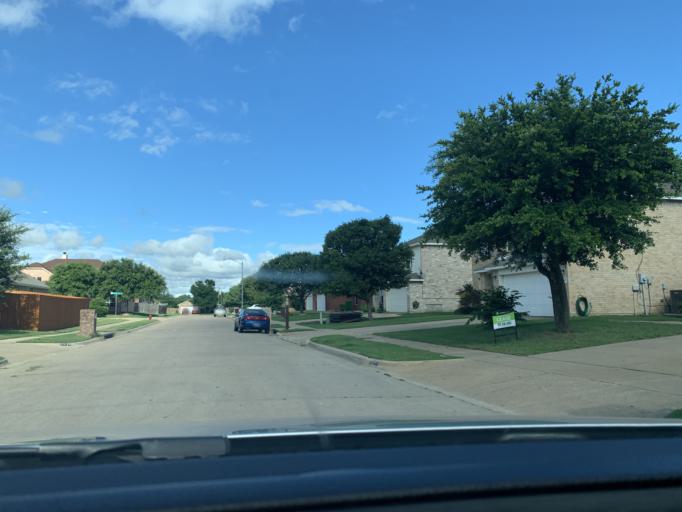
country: US
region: Texas
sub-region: Dallas County
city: Cedar Hill
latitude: 32.6430
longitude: -97.0326
